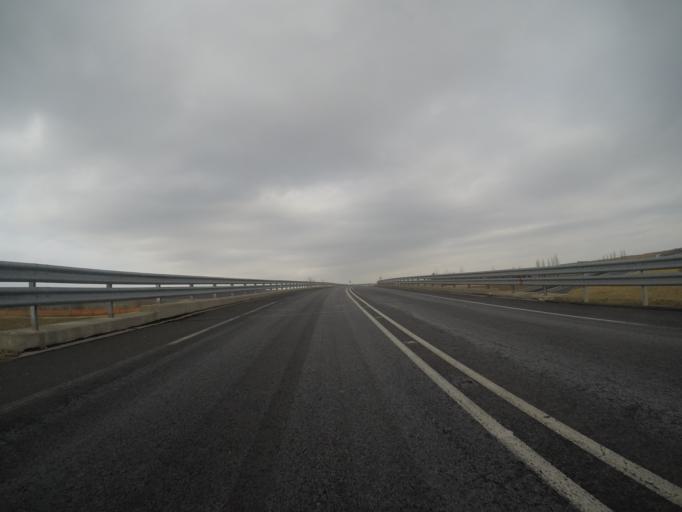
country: HU
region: Zala
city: Nagykanizsa
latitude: 46.4765
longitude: 17.0309
